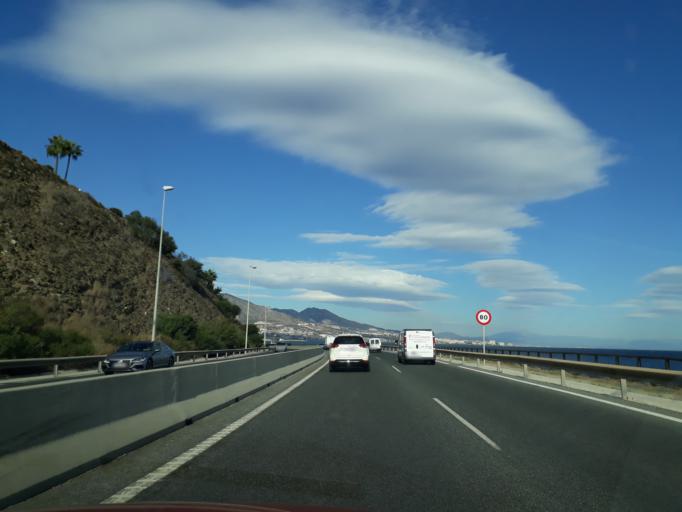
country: ES
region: Andalusia
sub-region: Provincia de Malaga
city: Fuengirola
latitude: 36.5167
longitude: -4.6314
